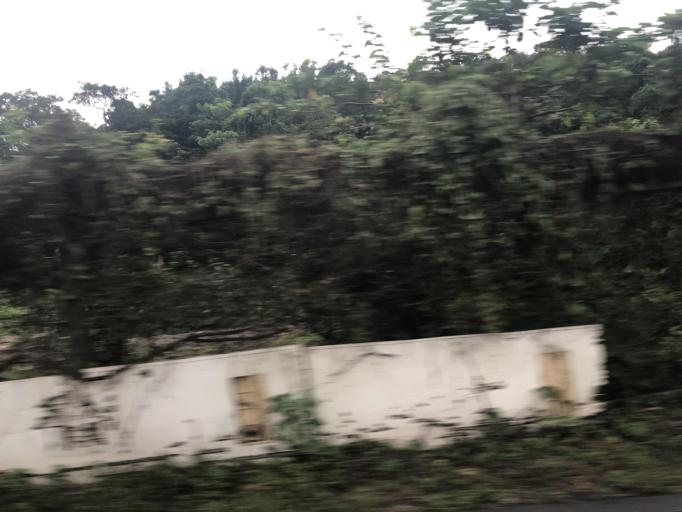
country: TW
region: Taiwan
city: Daxi
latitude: 24.9178
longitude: 121.3532
